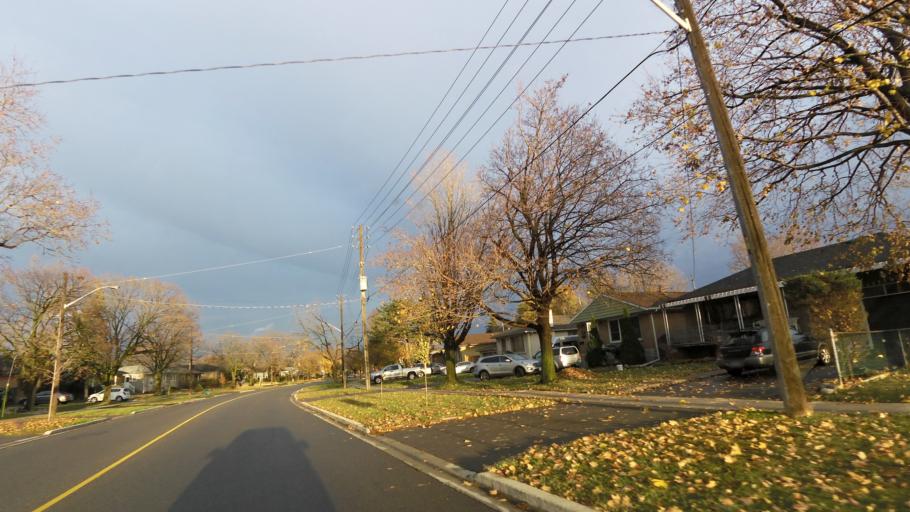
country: CA
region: Ontario
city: Etobicoke
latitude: 43.6609
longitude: -79.5805
